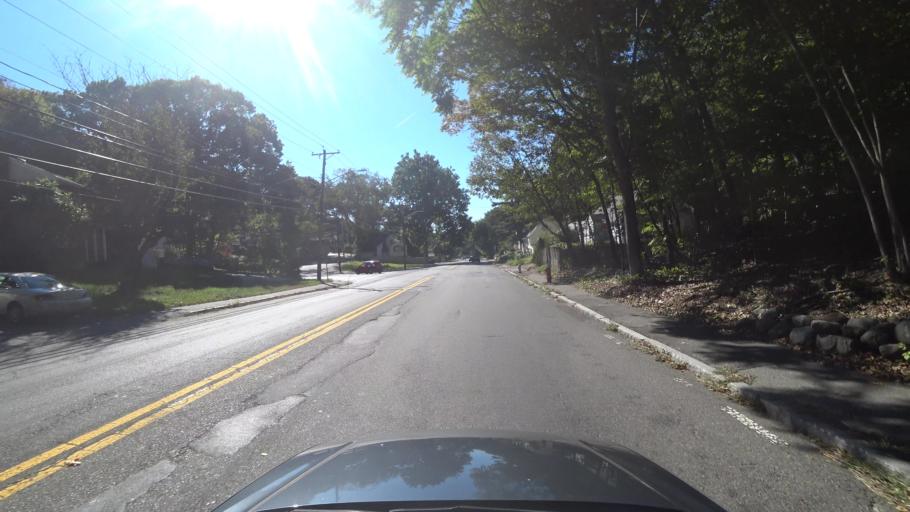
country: US
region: Massachusetts
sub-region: Essex County
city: Swampscott
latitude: 42.4772
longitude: -70.9097
